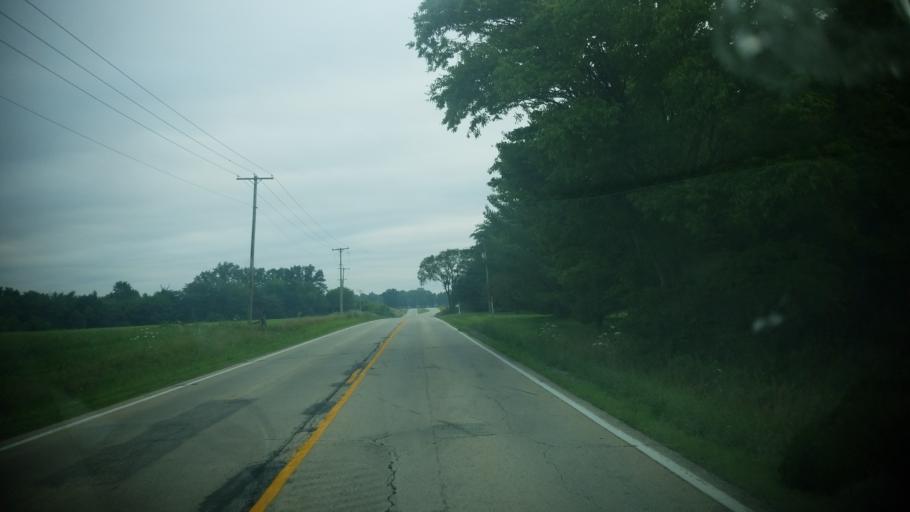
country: US
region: Illinois
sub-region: Clay County
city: Flora
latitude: 38.6670
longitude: -88.4383
